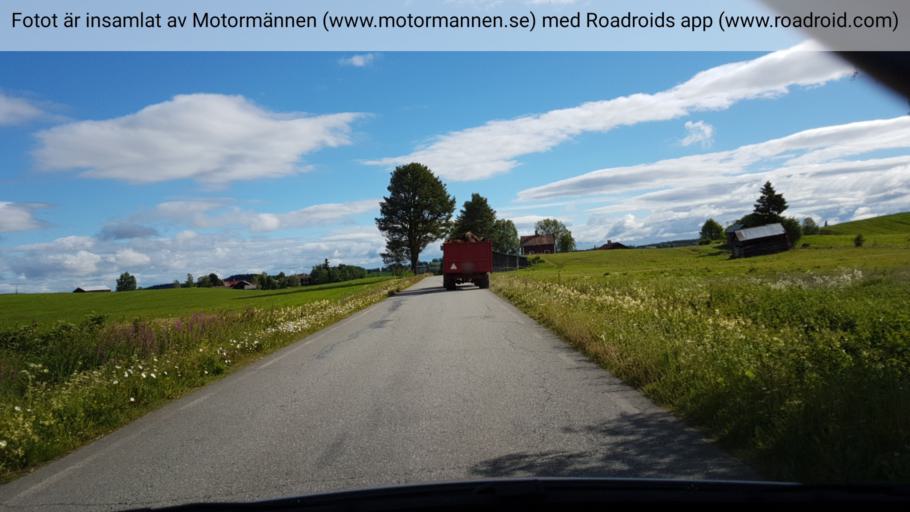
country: SE
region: Jaemtland
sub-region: Krokoms Kommun
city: Krokom
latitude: 63.2940
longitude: 14.4501
